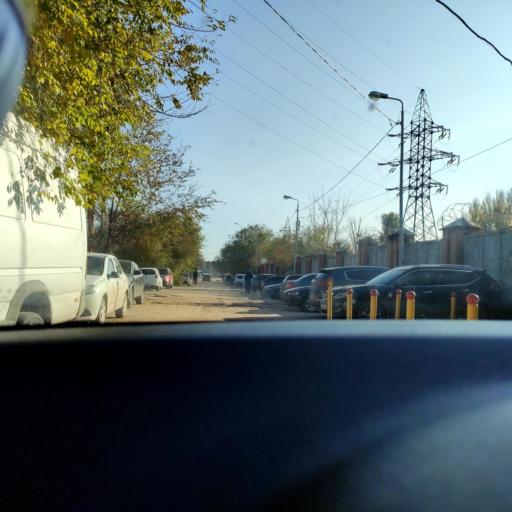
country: RU
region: Samara
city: Smyshlyayevka
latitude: 53.2095
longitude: 50.2721
